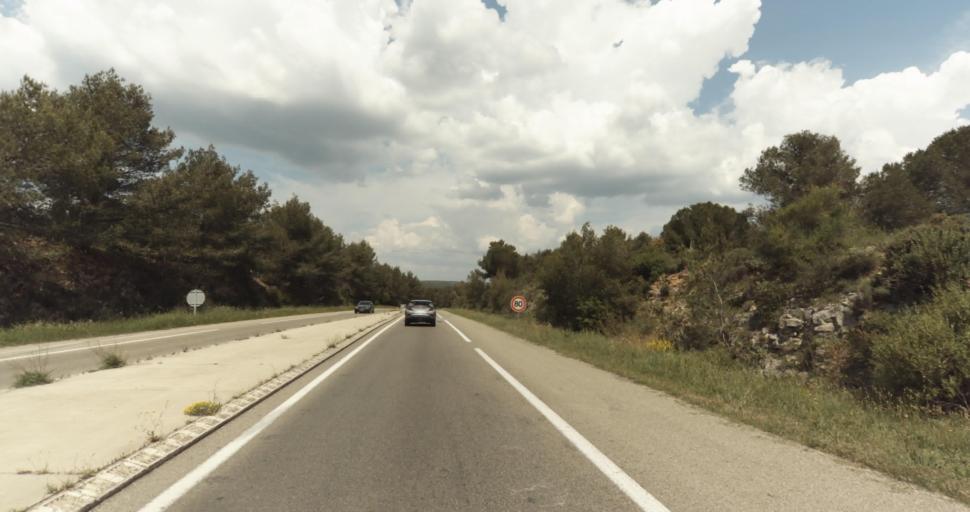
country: FR
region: Languedoc-Roussillon
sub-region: Departement du Gard
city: Nimes
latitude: 43.8607
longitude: 4.3238
